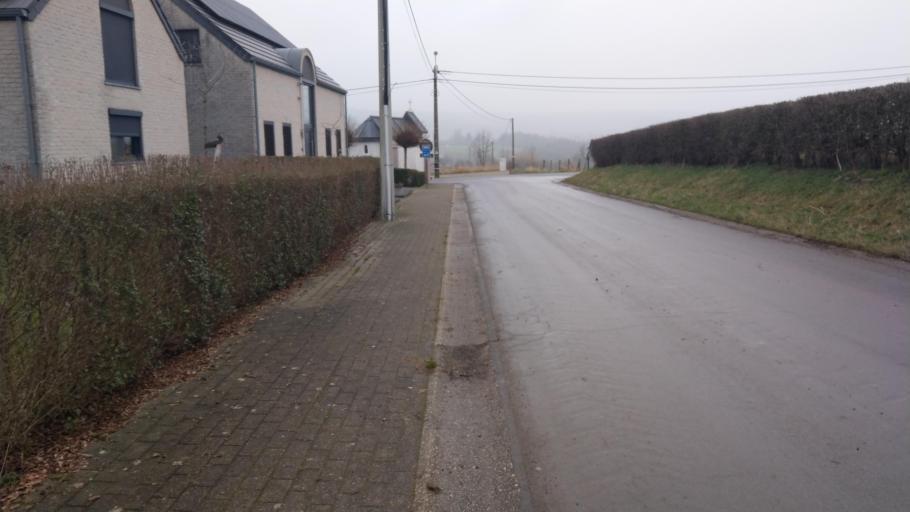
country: BE
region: Wallonia
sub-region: Province de Liege
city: Plombieres
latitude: 50.7451
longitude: 5.9377
